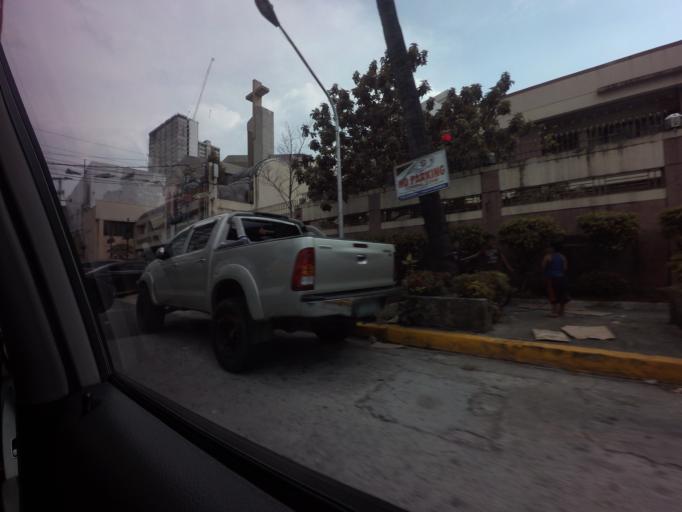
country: PH
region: Metro Manila
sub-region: San Juan
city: San Juan
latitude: 14.6036
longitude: 121.0132
